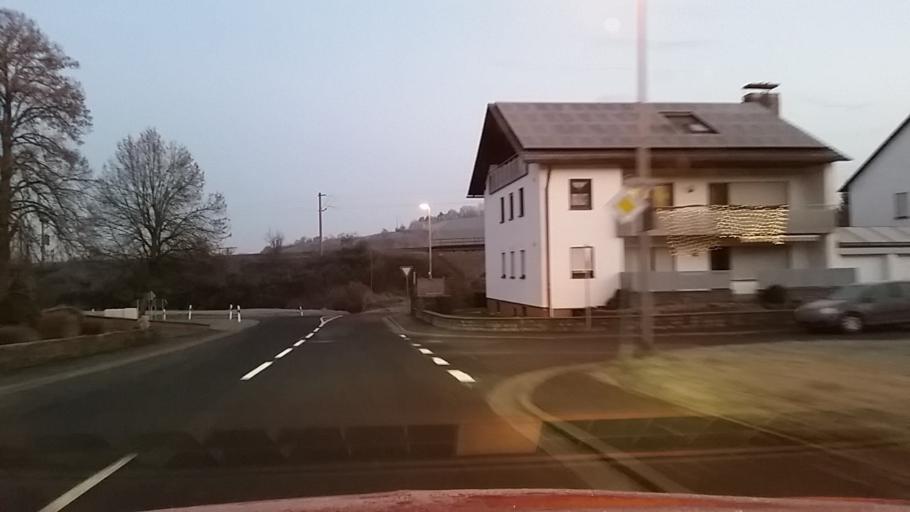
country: DE
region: Bavaria
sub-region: Regierungsbezirk Unterfranken
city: Thungen
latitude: 49.9444
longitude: 9.8274
